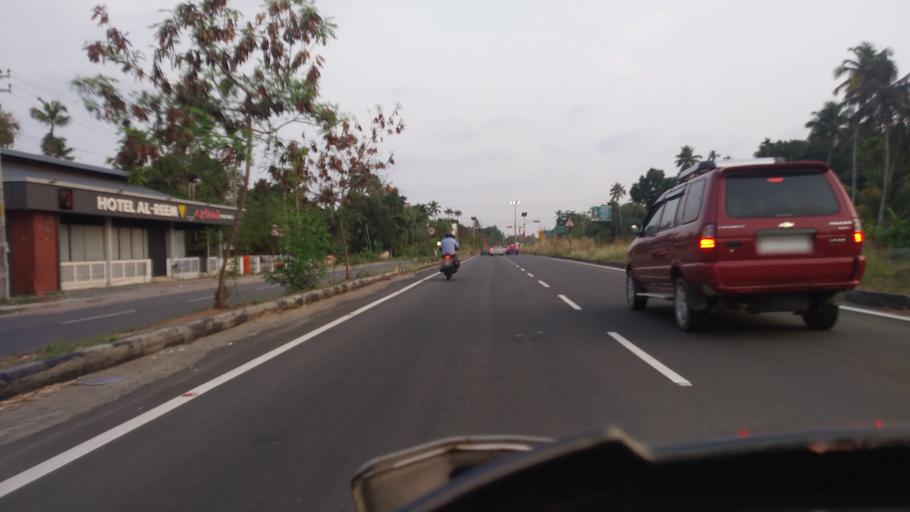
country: IN
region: Kerala
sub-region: Thrissur District
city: Kodungallur
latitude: 10.2141
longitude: 76.1979
